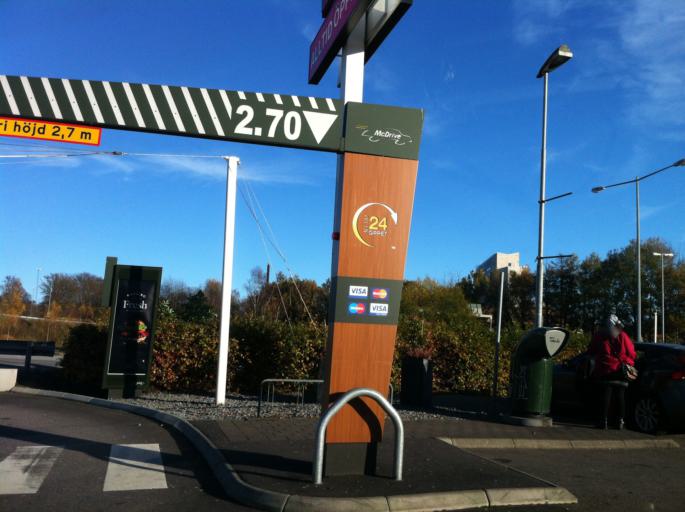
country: SE
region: Blekinge
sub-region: Karlshamns Kommun
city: Karlshamn
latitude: 56.1889
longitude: 14.8465
